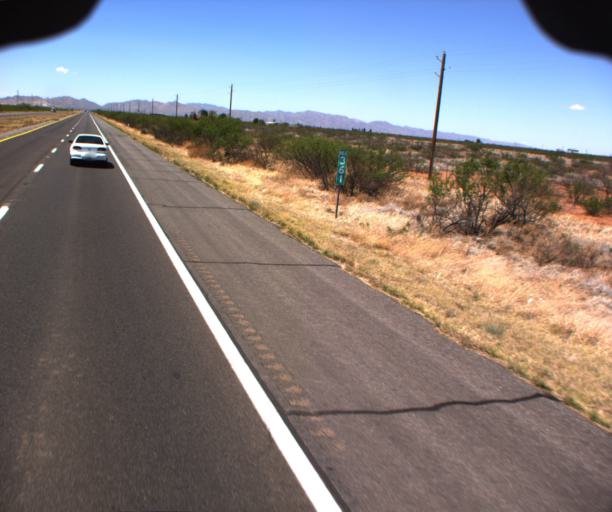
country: US
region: Arizona
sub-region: Cochise County
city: Pirtleville
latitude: 31.3583
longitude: -109.6408
